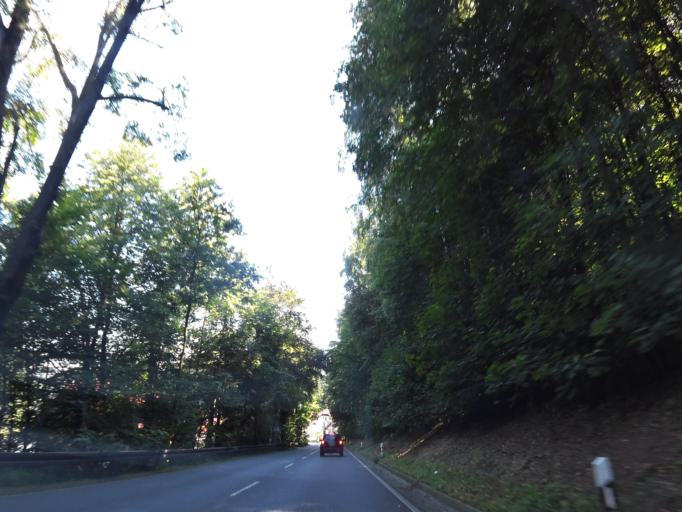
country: DE
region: Saxony
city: Konigstein
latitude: 50.9208
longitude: 14.0632
